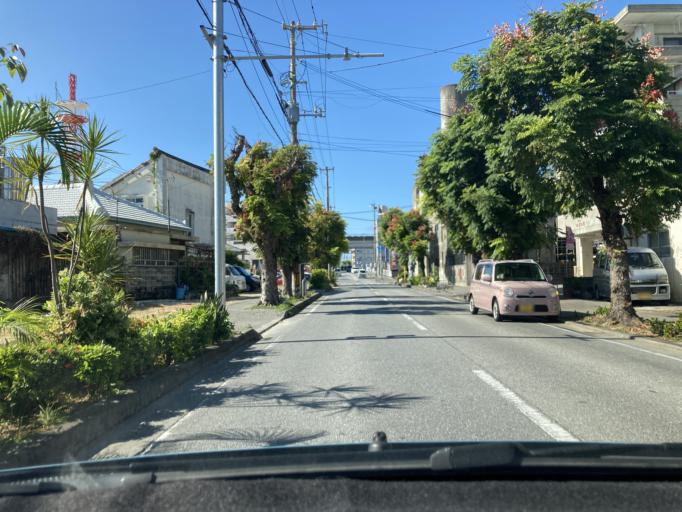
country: JP
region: Okinawa
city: Naha-shi
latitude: 26.2421
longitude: 127.6934
